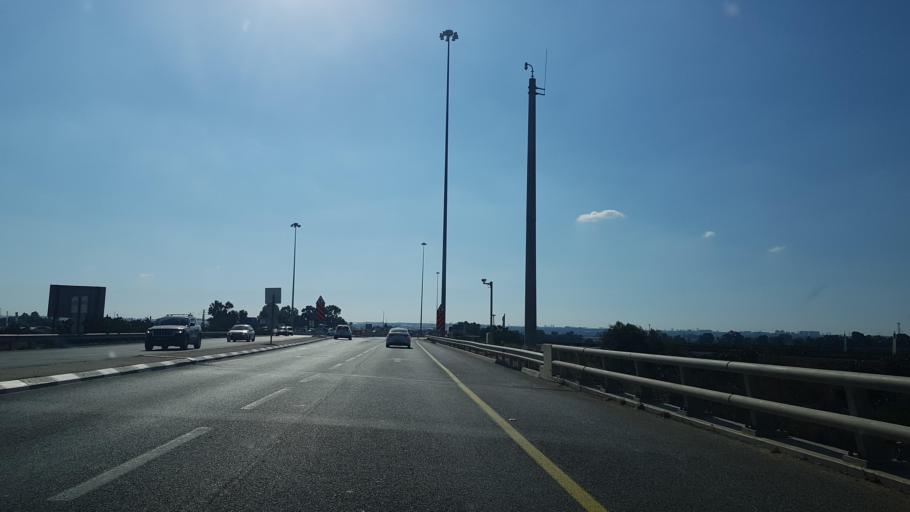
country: PS
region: West Bank
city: Tulkarm
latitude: 32.3137
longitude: 35.0125
